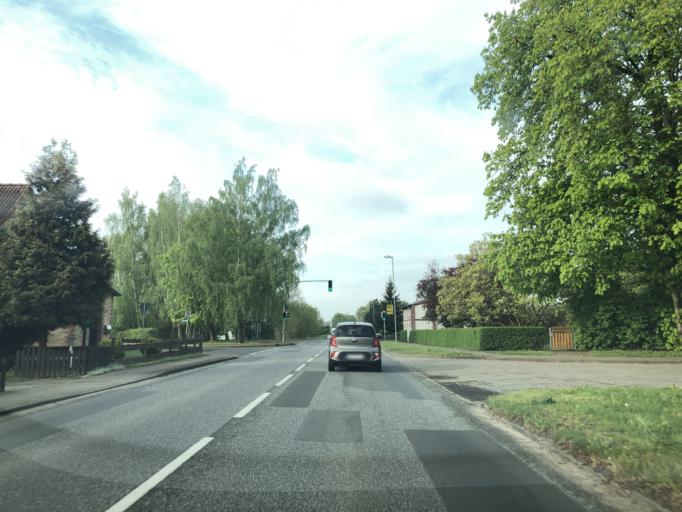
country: DE
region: Mecklenburg-Vorpommern
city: Laage
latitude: 53.8850
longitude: 12.2497
